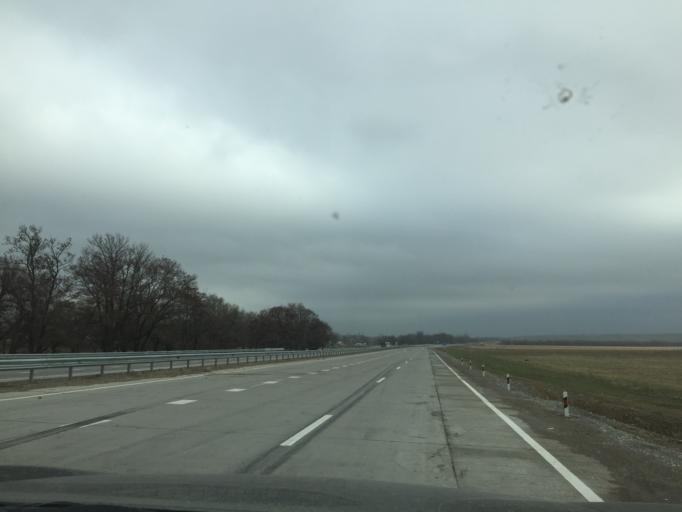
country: KZ
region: Ongtustik Qazaqstan
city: Kokterek
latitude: 42.5550
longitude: 70.1400
